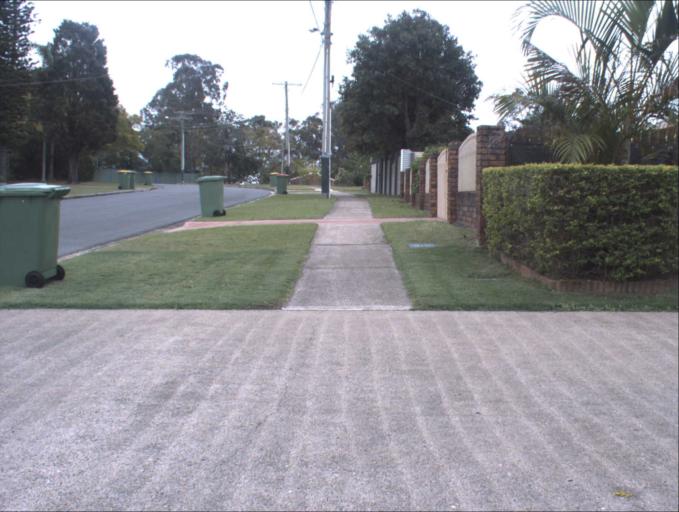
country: AU
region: Queensland
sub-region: Logan
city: Park Ridge South
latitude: -27.6873
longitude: 153.0200
